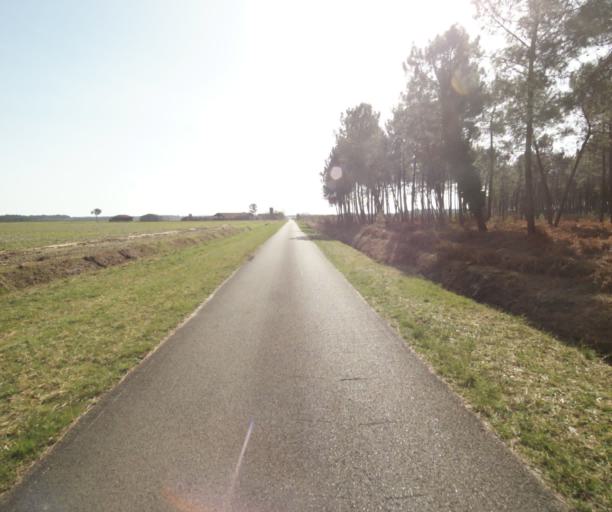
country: FR
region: Aquitaine
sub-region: Departement des Landes
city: Roquefort
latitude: 44.1634
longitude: -0.2511
